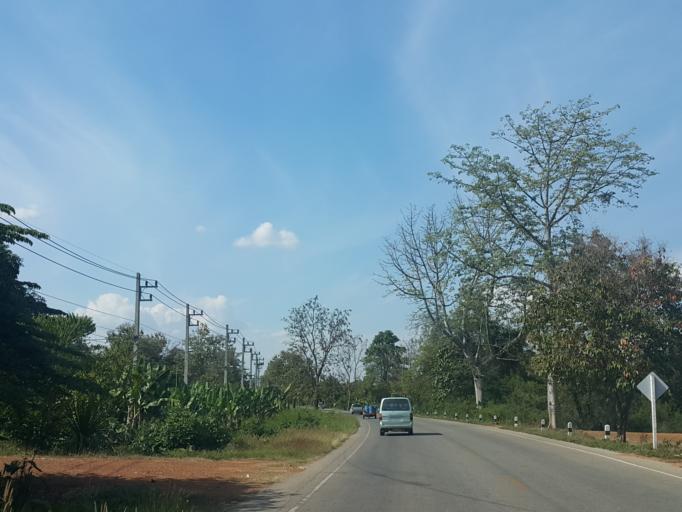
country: TH
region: Sukhothai
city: Sawankhalok
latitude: 17.2543
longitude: 99.8420
